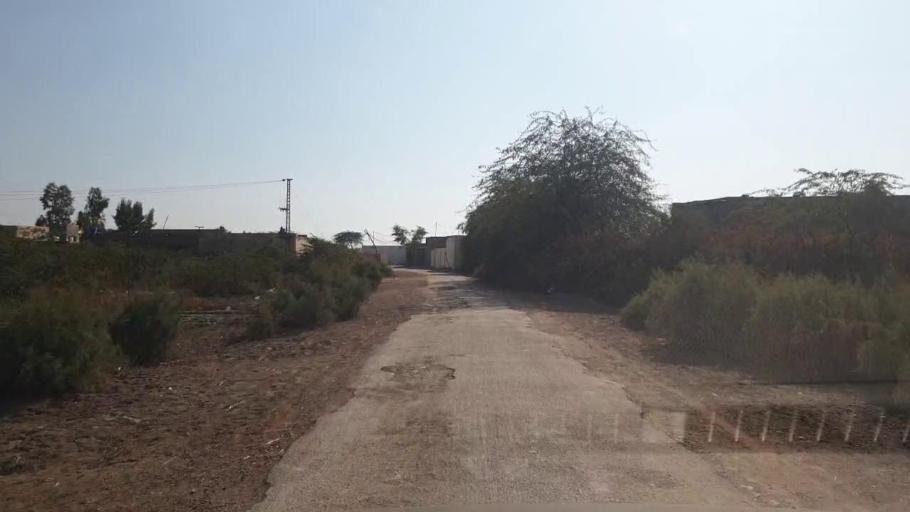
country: PK
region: Sindh
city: Shahpur Chakar
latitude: 26.1527
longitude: 68.6709
